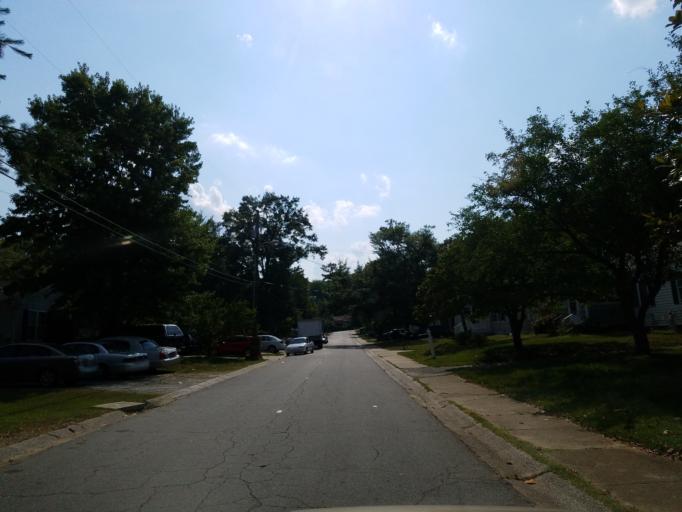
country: US
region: Georgia
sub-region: Cobb County
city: Marietta
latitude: 33.9578
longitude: -84.5396
